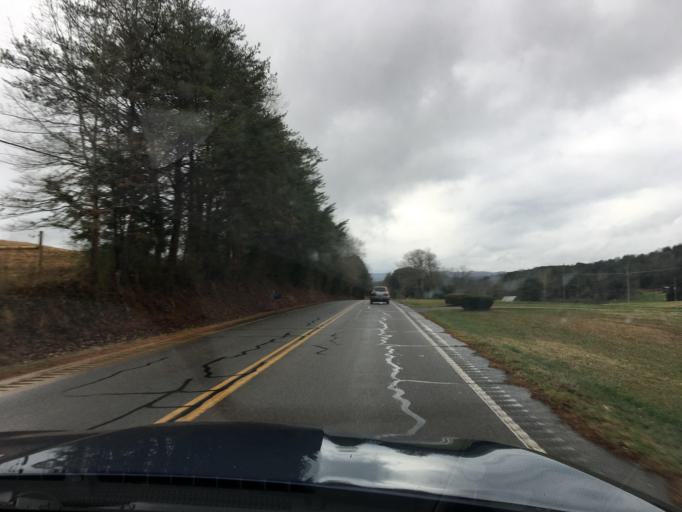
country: US
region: Tennessee
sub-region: Polk County
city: Benton
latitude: 35.1195
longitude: -84.6512
